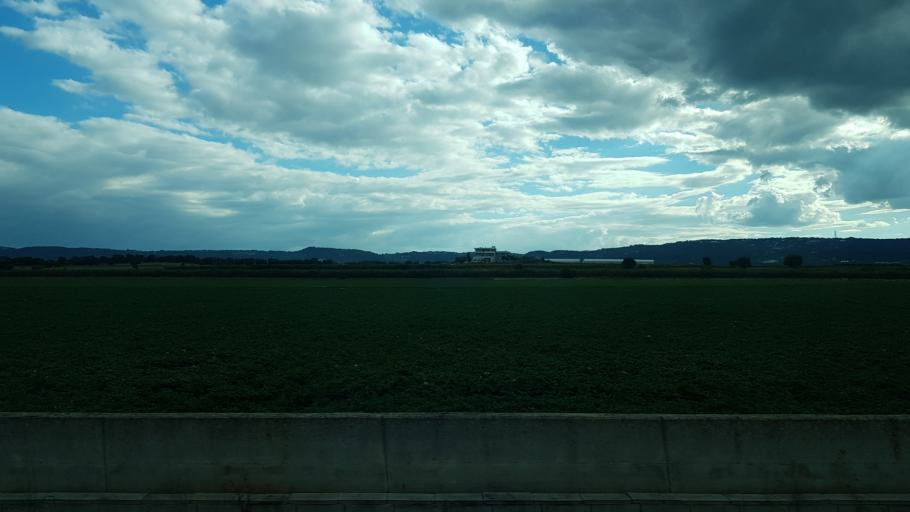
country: IT
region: Apulia
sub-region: Provincia di Brindisi
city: Fasano
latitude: 40.8465
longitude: 17.3935
